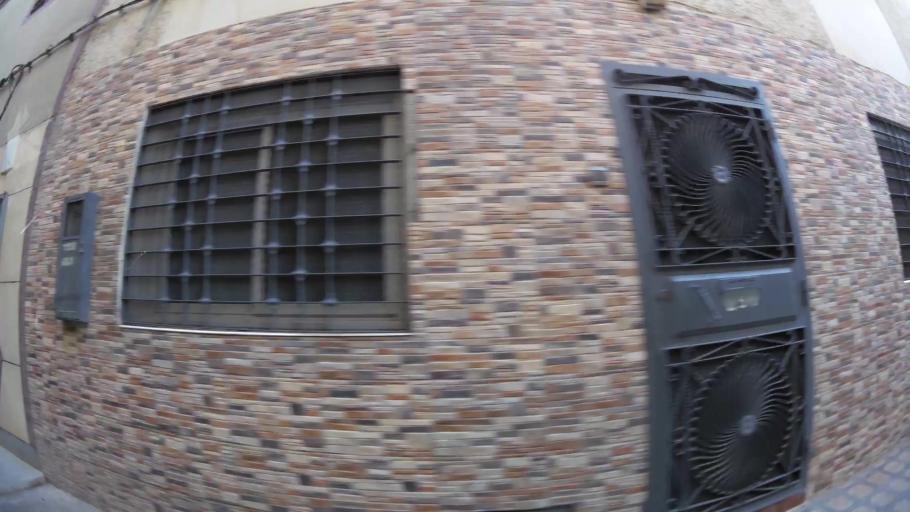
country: MA
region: Oriental
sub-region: Oujda-Angad
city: Oujda
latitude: 34.6939
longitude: -1.9041
